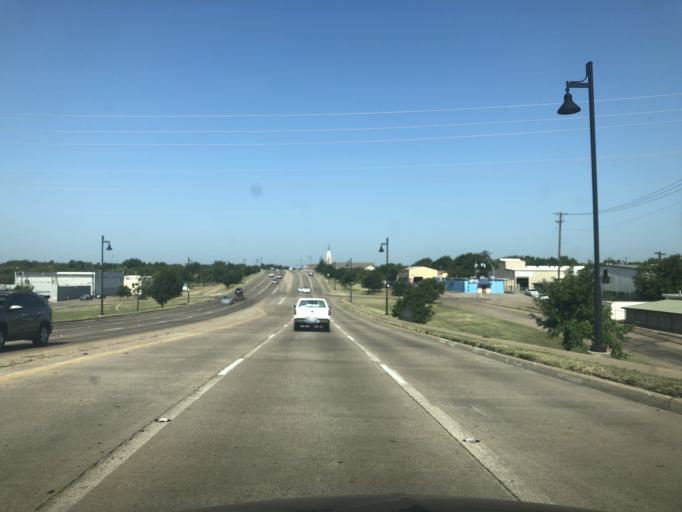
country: US
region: Texas
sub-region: Tarrant County
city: Fort Worth
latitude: 32.7060
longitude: -97.3248
